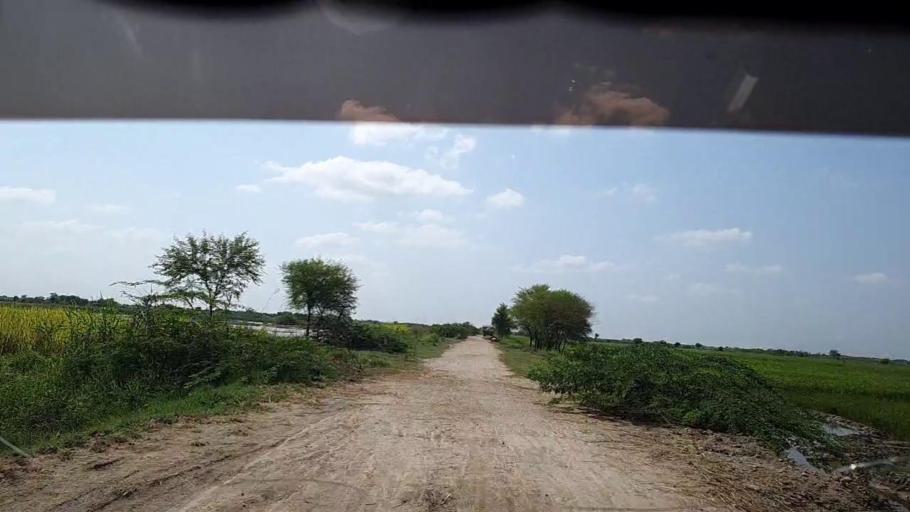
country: PK
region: Sindh
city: Kadhan
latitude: 24.5938
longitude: 69.0302
